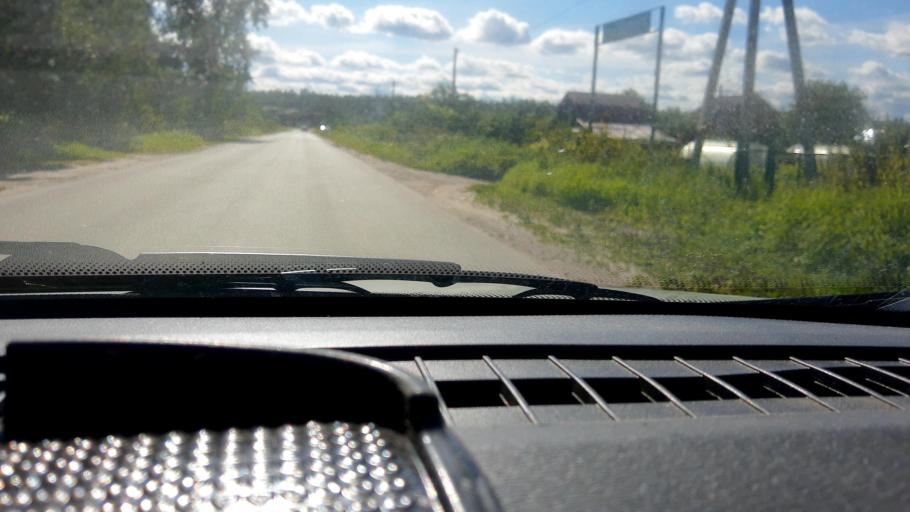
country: RU
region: Nizjnij Novgorod
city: Lukino
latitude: 56.4178
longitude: 43.6439
